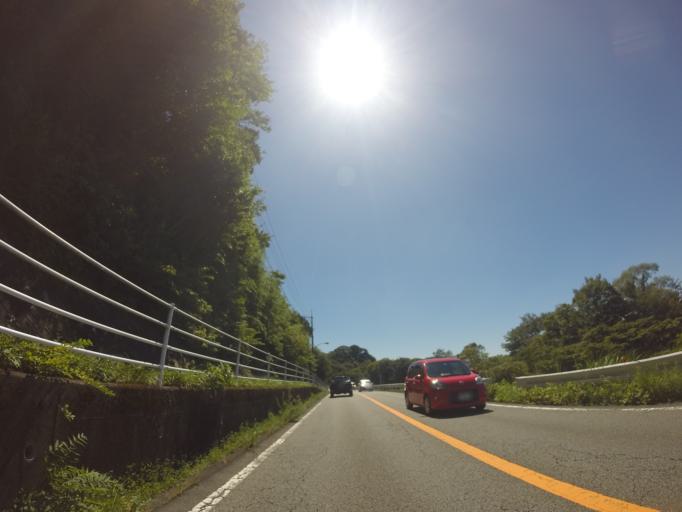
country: JP
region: Shizuoka
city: Kanaya
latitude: 34.8463
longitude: 138.1443
